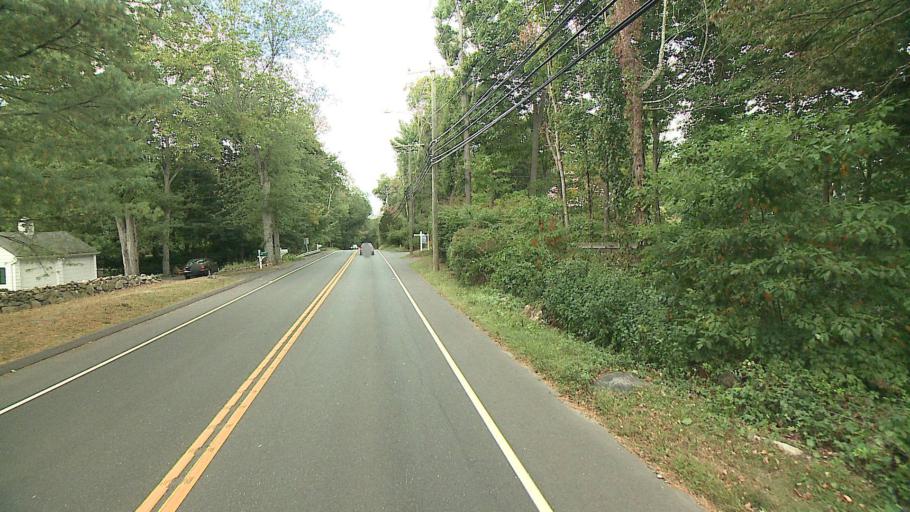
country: US
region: Connecticut
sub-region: Fairfield County
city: Westport
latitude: 41.1562
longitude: -73.3719
